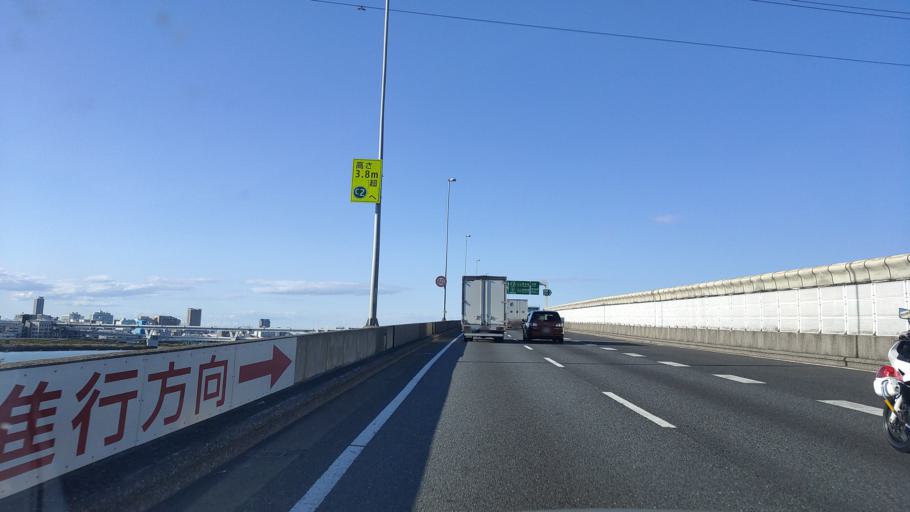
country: JP
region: Saitama
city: Soka
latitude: 35.7398
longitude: 139.8249
